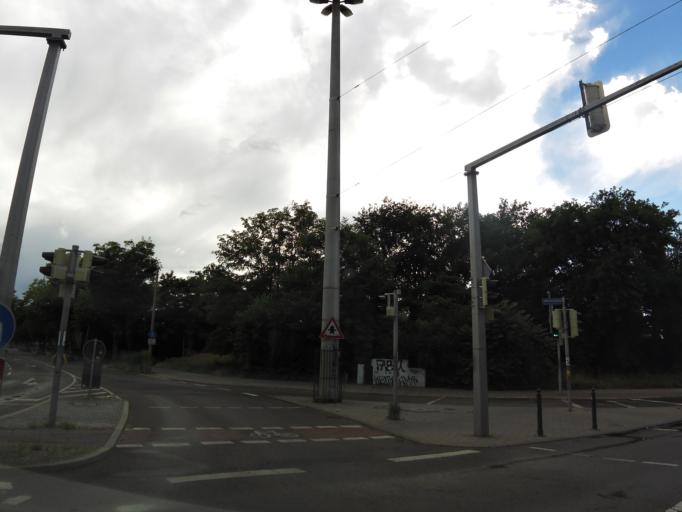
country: DE
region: Saxony
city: Leipzig
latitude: 51.3322
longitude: 12.3950
